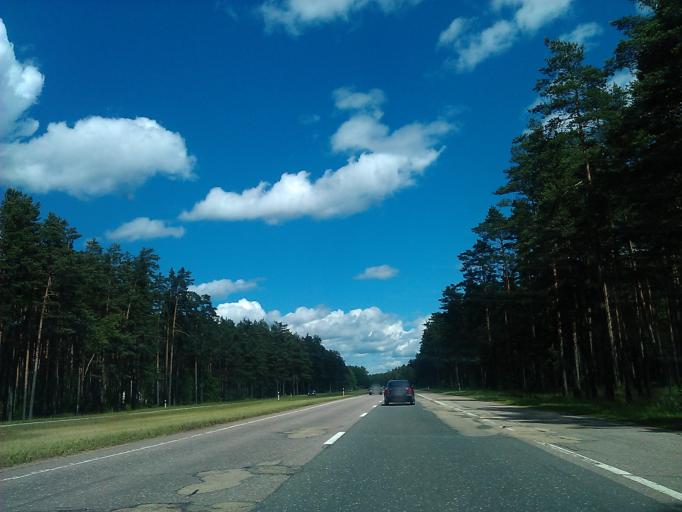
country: LV
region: Garkalne
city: Garkalne
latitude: 57.0440
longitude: 24.4290
